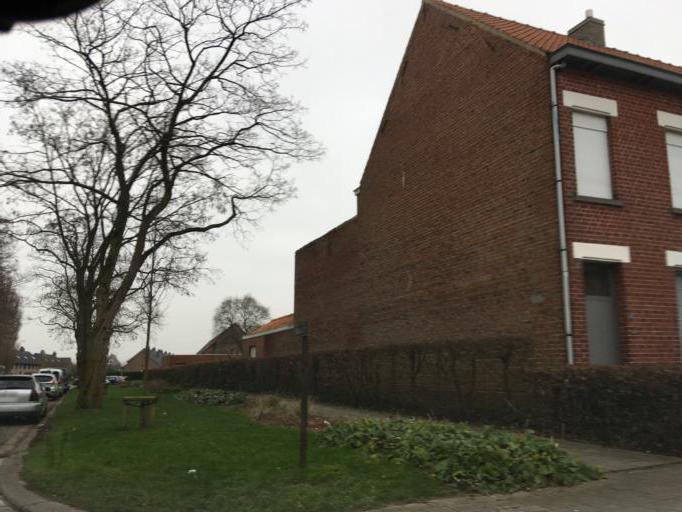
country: BE
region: Flanders
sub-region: Provincie West-Vlaanderen
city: Roeselare
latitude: 50.9662
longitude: 3.1369
